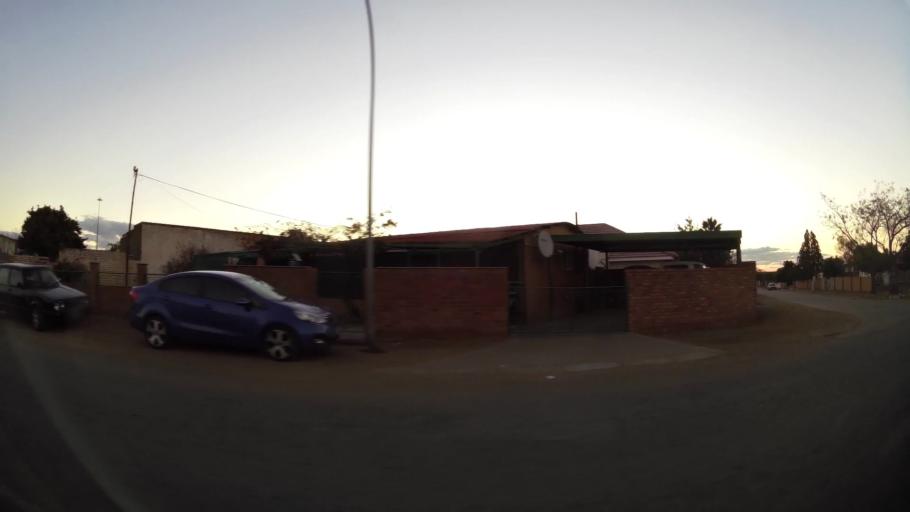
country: ZA
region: Northern Cape
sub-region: Frances Baard District Municipality
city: Kimberley
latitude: -28.7211
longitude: 24.7675
